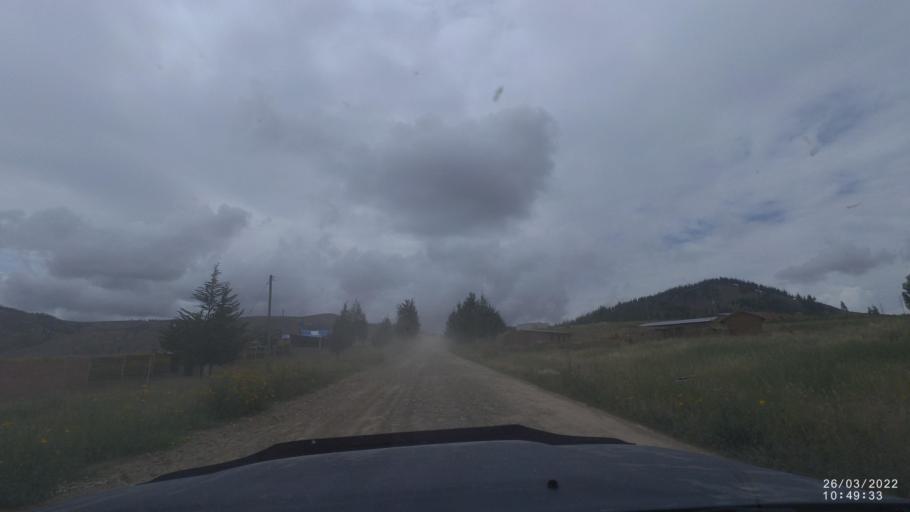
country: BO
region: Cochabamba
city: Tarata
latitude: -17.5032
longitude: -66.0365
